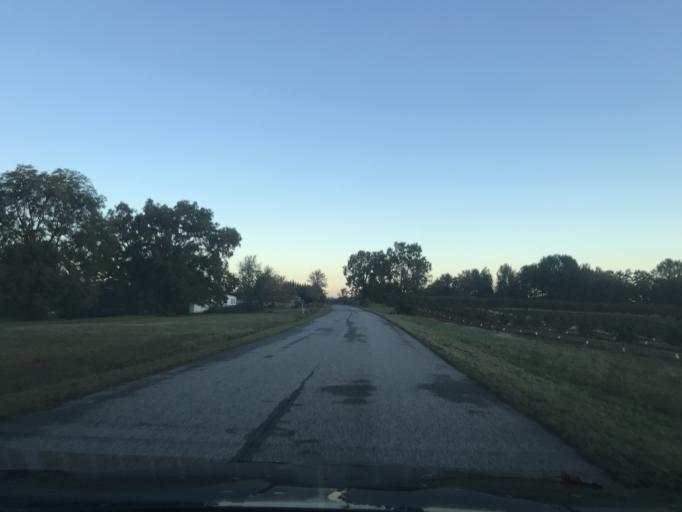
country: US
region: South Carolina
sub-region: Spartanburg County
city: Mayo
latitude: 35.1268
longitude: -81.7752
